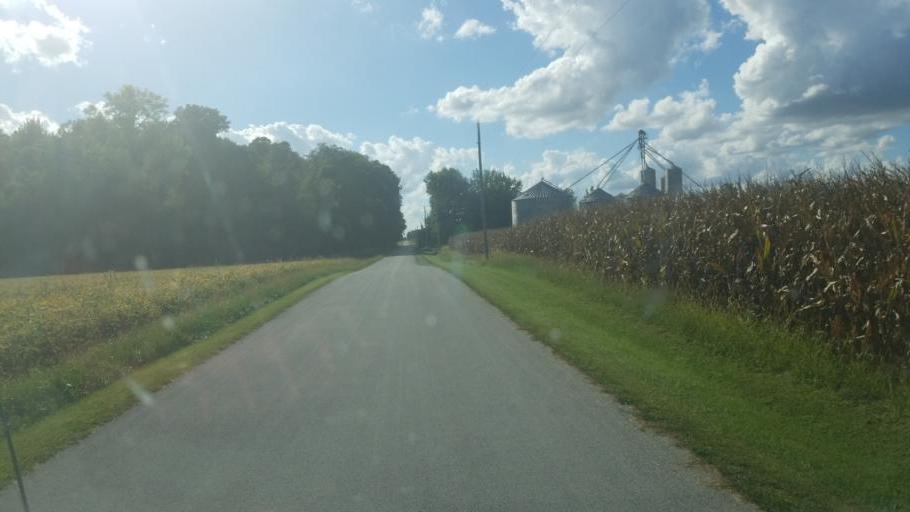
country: US
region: Ohio
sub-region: Hardin County
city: Kenton
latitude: 40.7181
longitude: -83.7022
